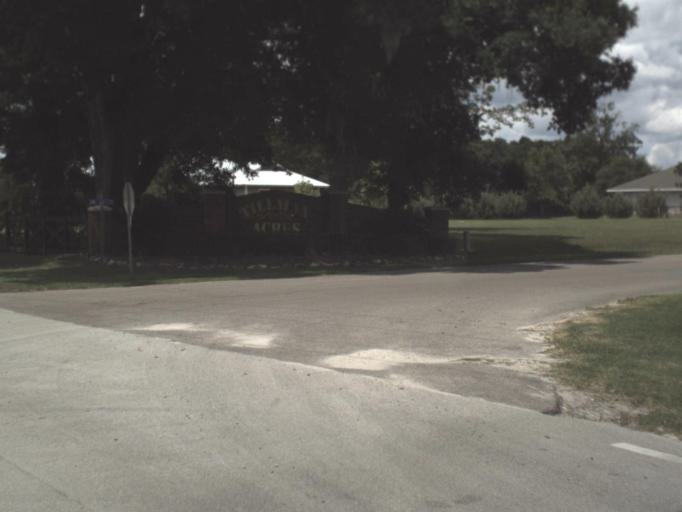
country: US
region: Florida
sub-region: Alachua County
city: High Springs
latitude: 29.8019
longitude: -82.6084
